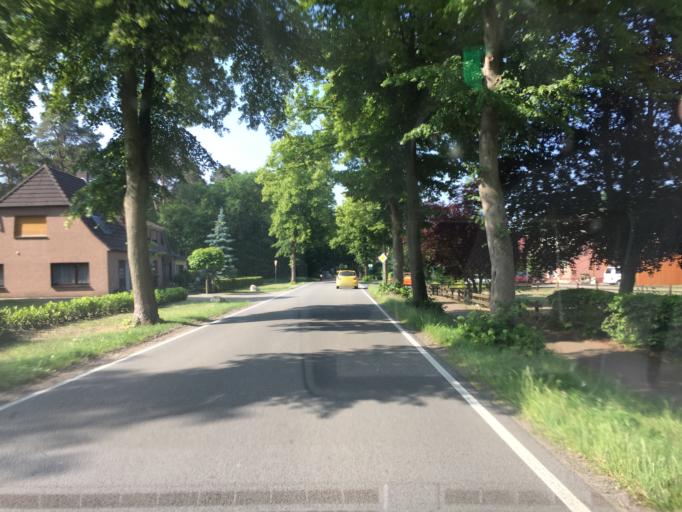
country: DE
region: Lower Saxony
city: Bahrenborstel
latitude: 52.5752
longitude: 8.8194
